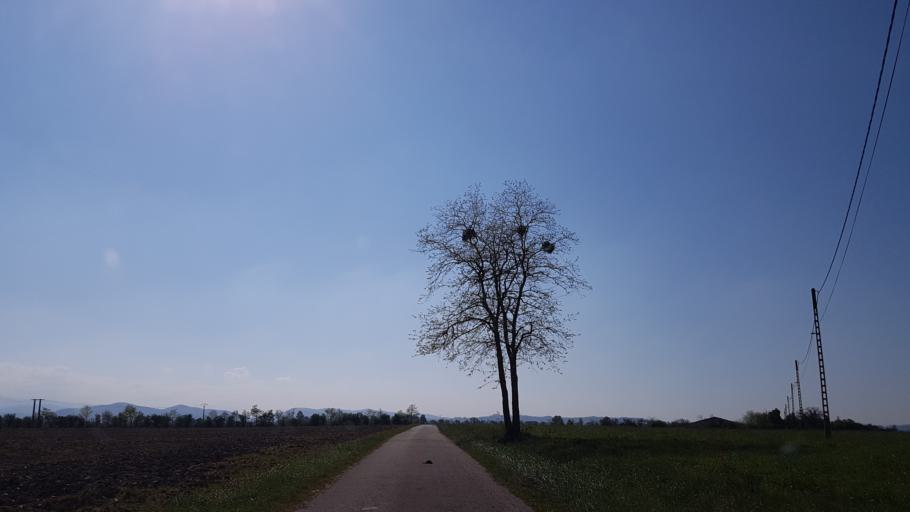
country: FR
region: Midi-Pyrenees
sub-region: Departement de l'Ariege
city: La Tour-du-Crieu
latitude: 43.0872
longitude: 1.6985
